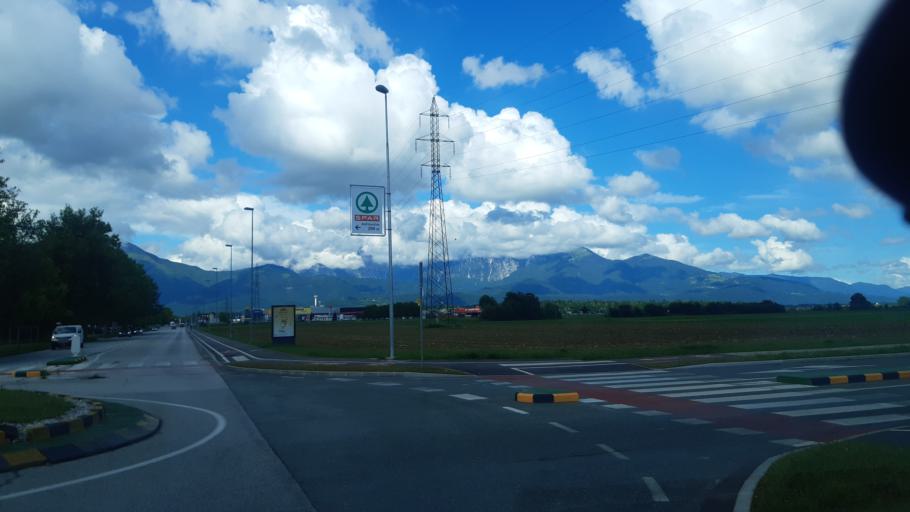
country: SI
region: Kranj
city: Kranj
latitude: 46.2383
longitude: 14.3703
